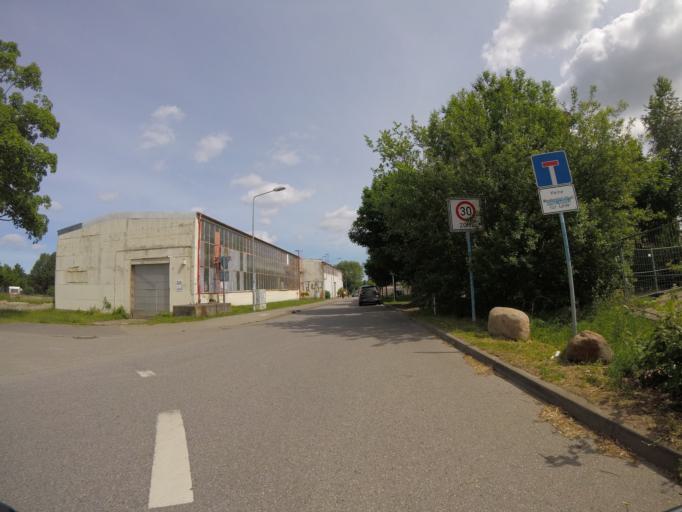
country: DE
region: Mecklenburg-Vorpommern
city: Rostock
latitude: 54.0956
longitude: 12.1052
